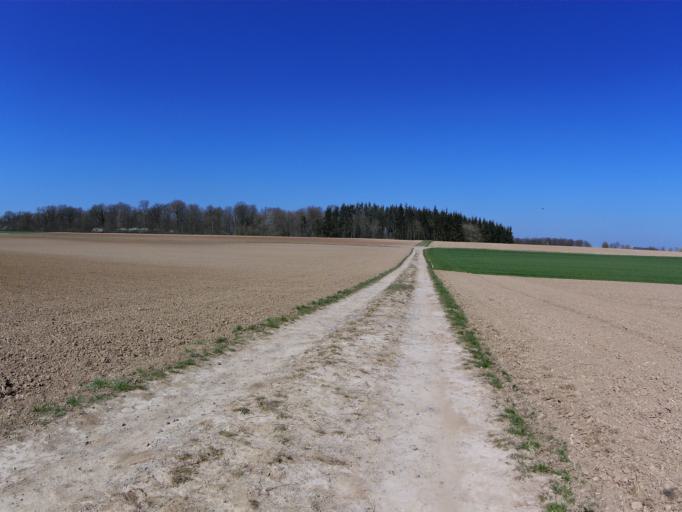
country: DE
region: Bavaria
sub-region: Regierungsbezirk Unterfranken
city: Kurnach
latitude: 49.8389
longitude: 10.0712
